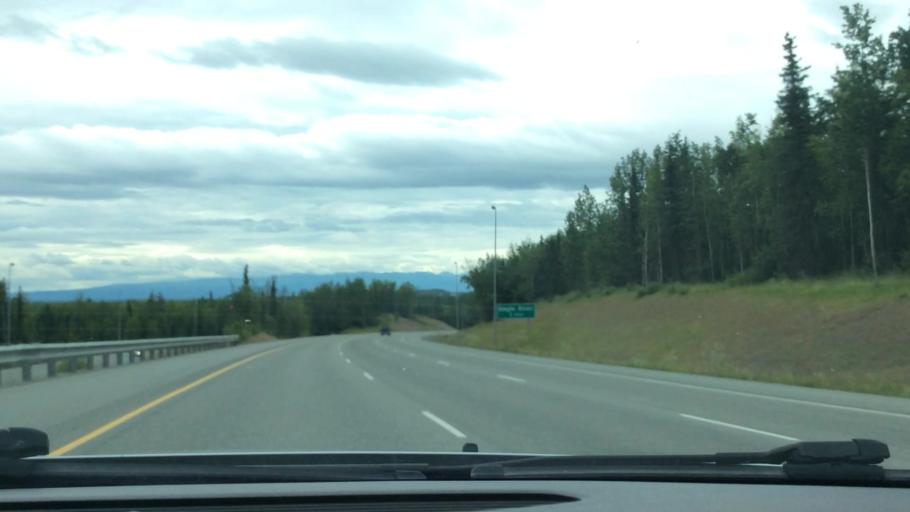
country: US
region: Alaska
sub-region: Anchorage Municipality
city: Eagle River
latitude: 61.3033
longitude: -149.5873
